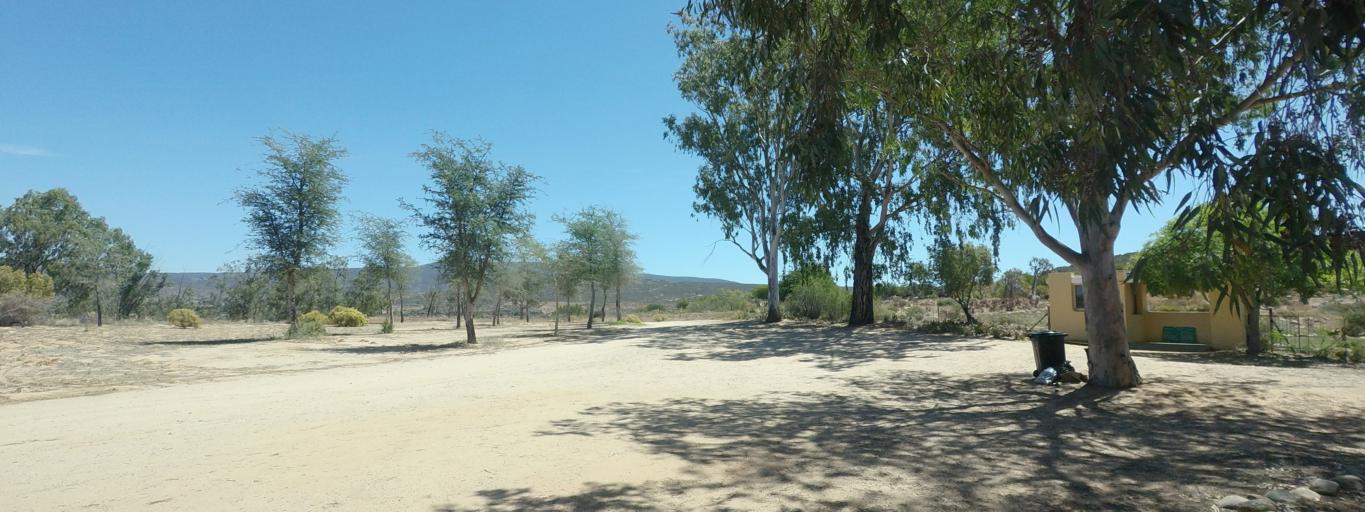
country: ZA
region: Western Cape
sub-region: West Coast District Municipality
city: Clanwilliam
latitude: -32.1867
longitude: 18.8839
